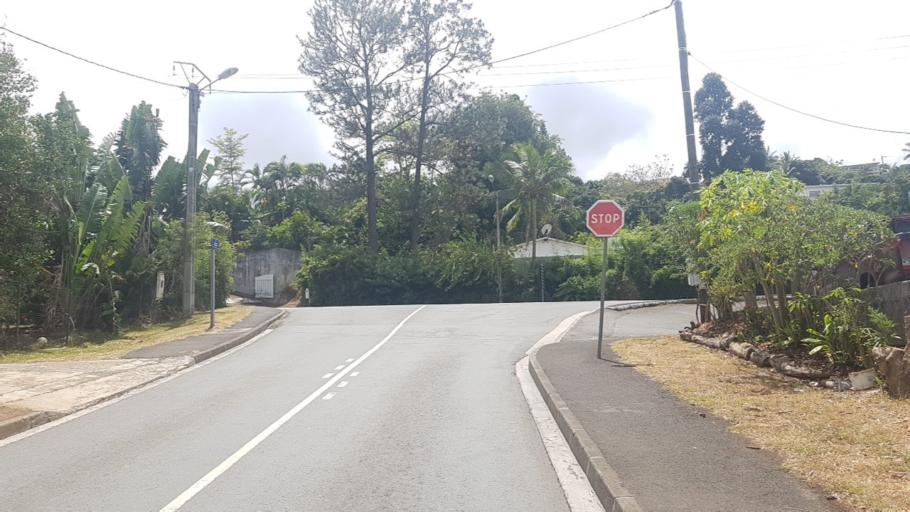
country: NC
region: South Province
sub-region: Dumbea
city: Dumbea
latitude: -22.2050
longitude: 166.4778
